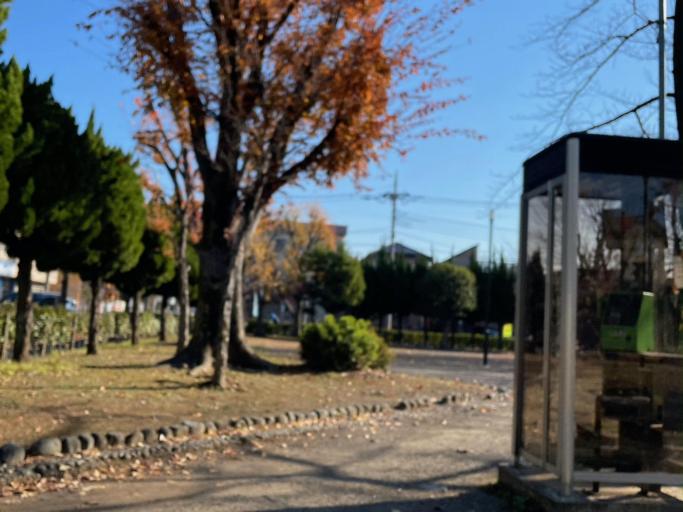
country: JP
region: Saitama
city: Soka
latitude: 35.8100
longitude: 139.8074
